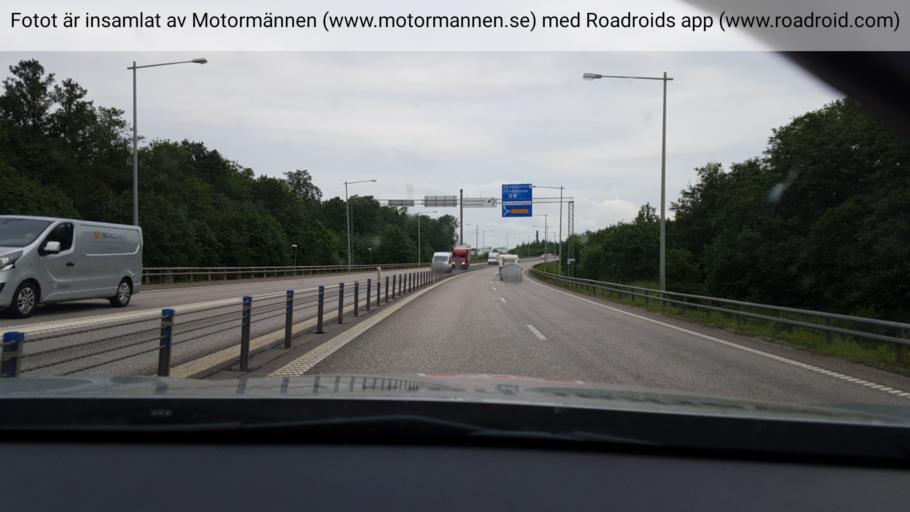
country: SE
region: Vaestra Goetaland
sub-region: Skovde Kommun
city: Skoevde
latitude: 58.3696
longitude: 13.8558
